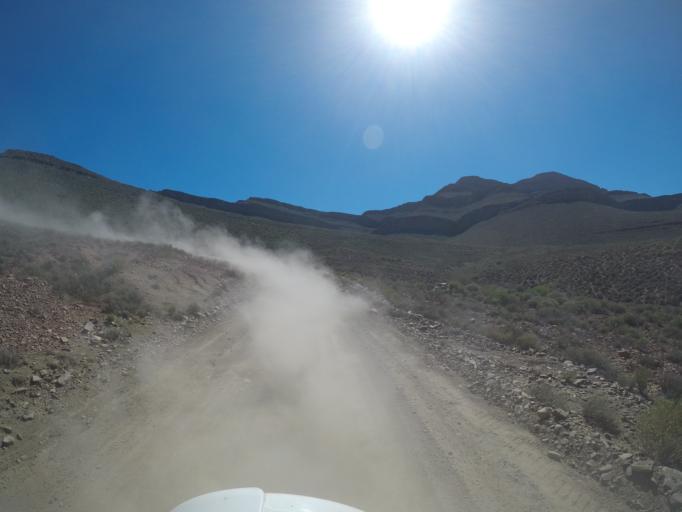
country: ZA
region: Western Cape
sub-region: West Coast District Municipality
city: Clanwilliam
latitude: -32.6193
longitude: 19.3842
